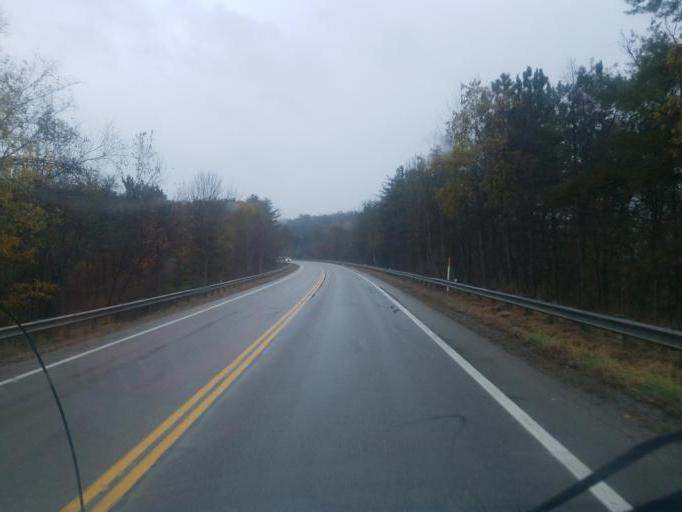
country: US
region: Ohio
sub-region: Muskingum County
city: North Zanesville
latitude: 40.0055
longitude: -82.0836
